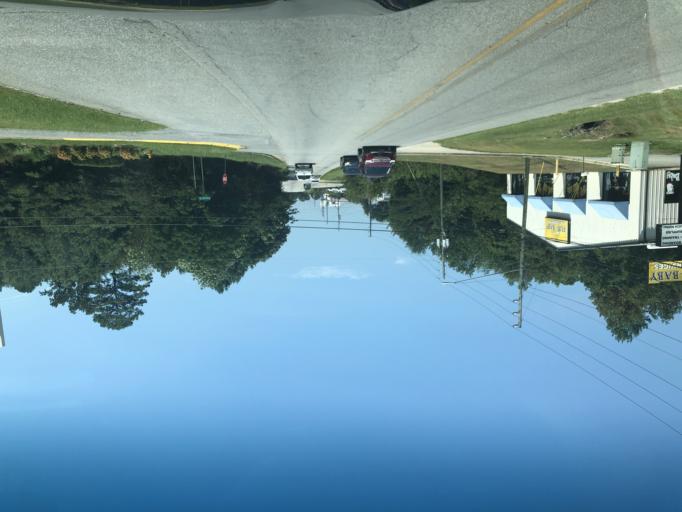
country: US
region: Georgia
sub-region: Muscogee County
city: Columbus
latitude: 32.5136
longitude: -84.9214
